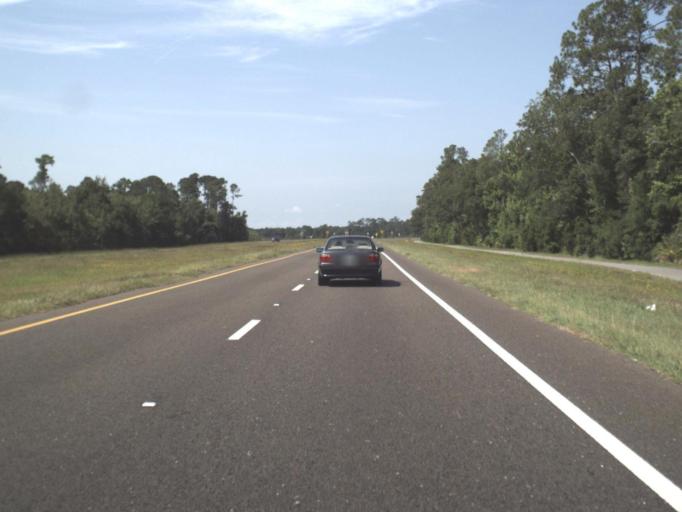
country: US
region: Florida
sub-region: Saint Johns County
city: Saint Augustine Shores
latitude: 29.7919
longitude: -81.4180
